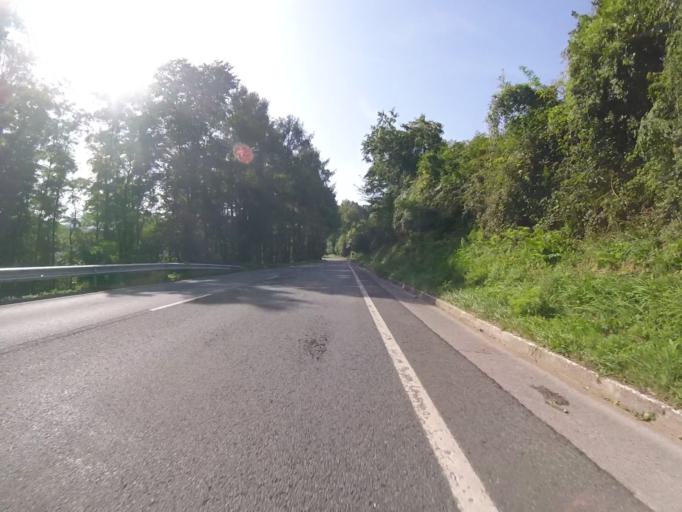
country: ES
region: Navarre
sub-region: Provincia de Navarra
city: Zugarramurdi
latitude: 43.2015
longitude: -1.4851
